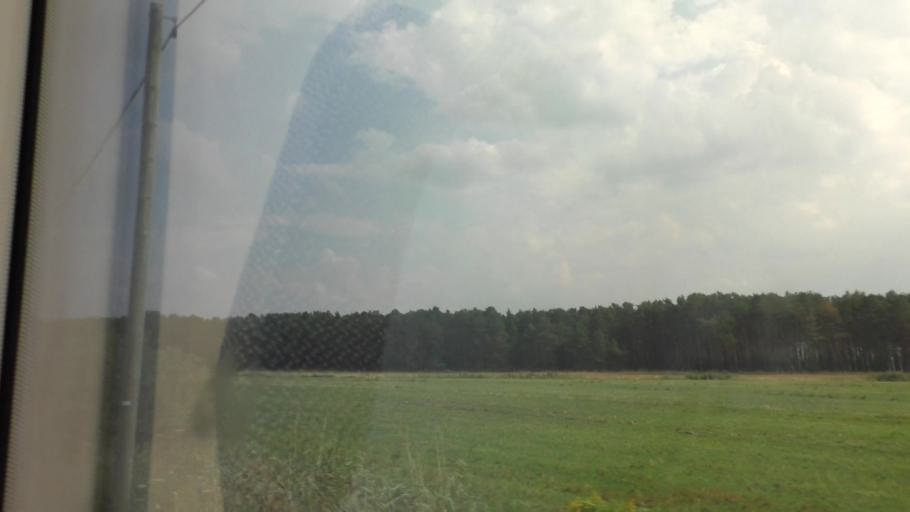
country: DE
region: Brandenburg
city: Spreenhagen
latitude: 52.2839
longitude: 13.8267
